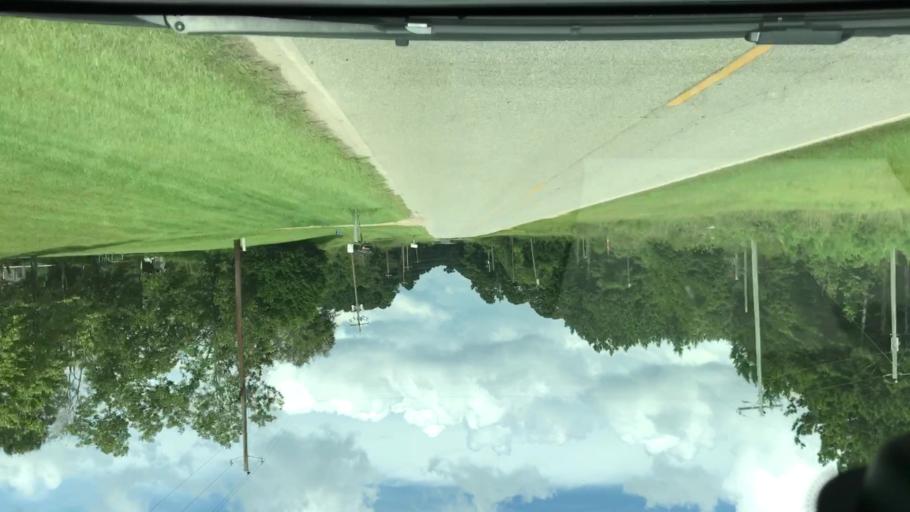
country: US
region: Georgia
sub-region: Clay County
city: Fort Gaines
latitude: 31.7196
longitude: -85.0541
